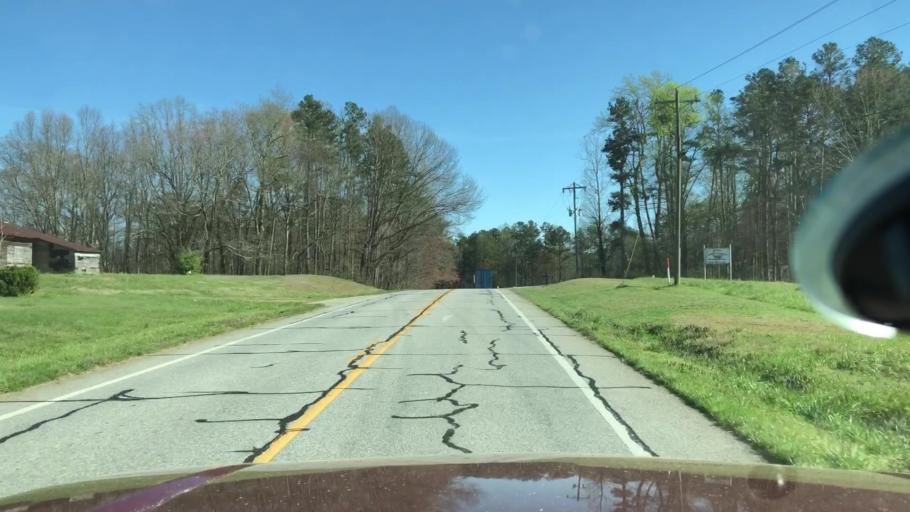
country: US
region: Georgia
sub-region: Dawson County
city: Dawsonville
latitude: 34.4492
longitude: -84.1687
